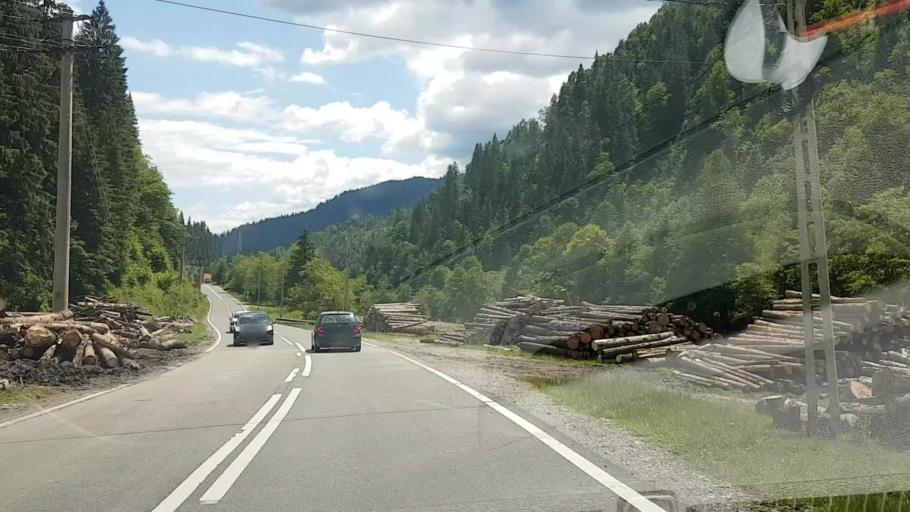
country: RO
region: Suceava
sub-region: Comuna Brosteni
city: Brosteni
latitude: 47.2727
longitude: 25.6484
